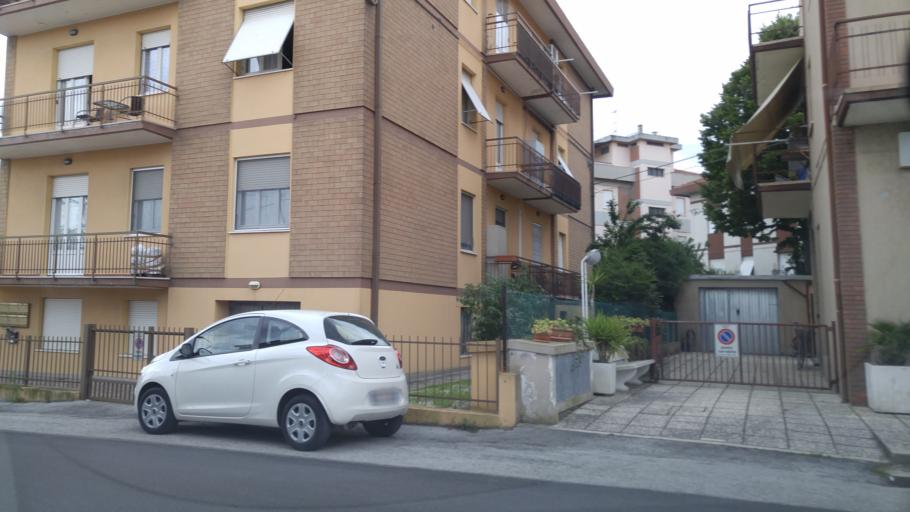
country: IT
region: The Marches
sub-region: Provincia di Pesaro e Urbino
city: Pesaro
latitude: 43.9177
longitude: 12.8993
